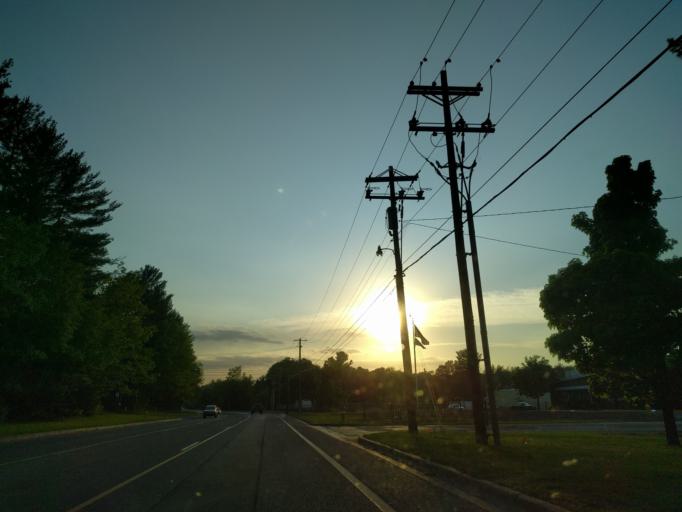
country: US
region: Michigan
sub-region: Marquette County
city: Trowbridge Park
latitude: 46.5647
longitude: -87.4360
